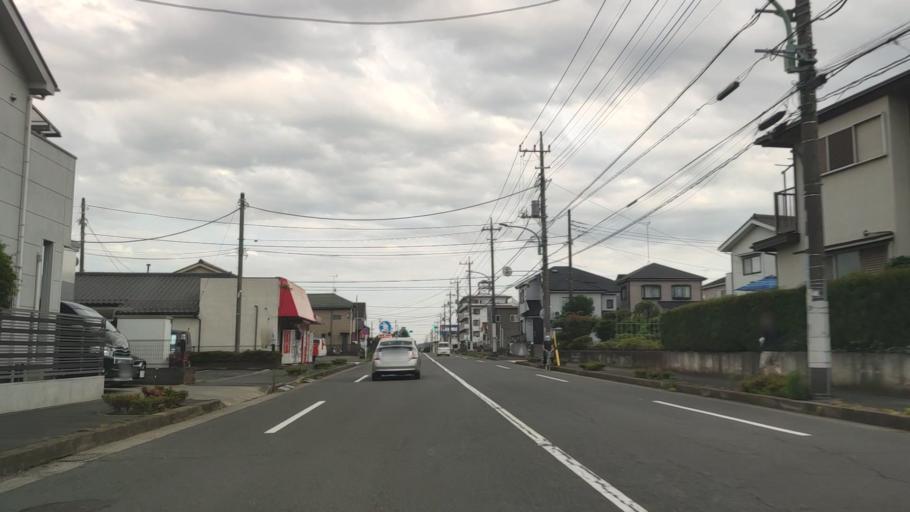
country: JP
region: Tokyo
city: Ome
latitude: 35.7944
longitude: 139.2986
